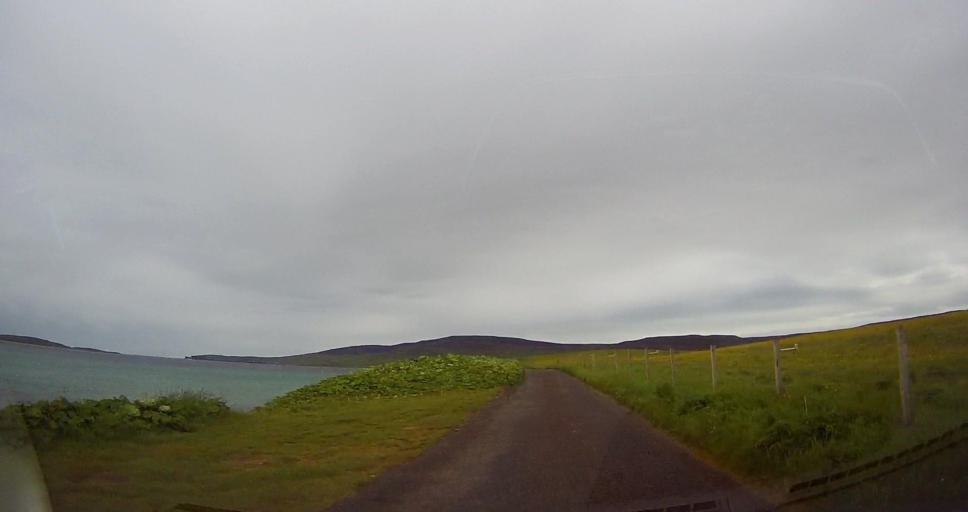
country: GB
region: Scotland
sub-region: Orkney Islands
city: Orkney
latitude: 59.1196
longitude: -3.0858
